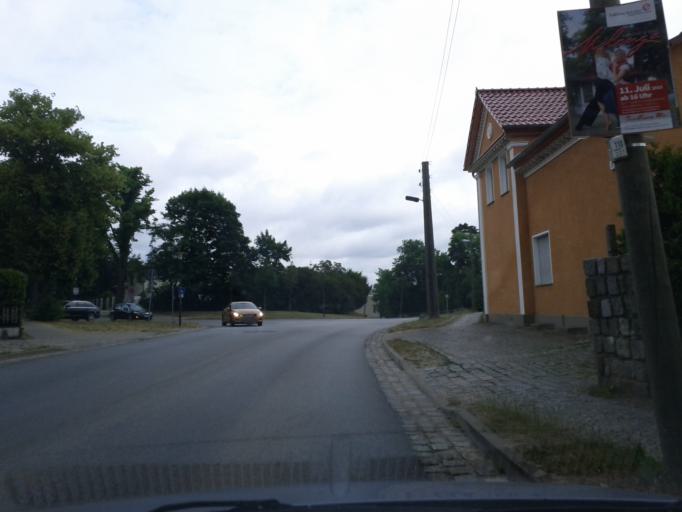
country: DE
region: Brandenburg
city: Woltersdorf
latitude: 52.4459
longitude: 13.7565
